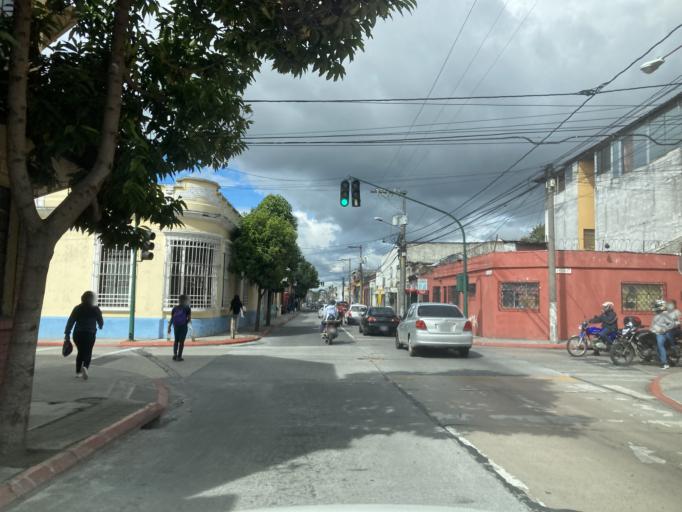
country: GT
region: Guatemala
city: Guatemala City
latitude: 14.6458
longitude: -90.5075
